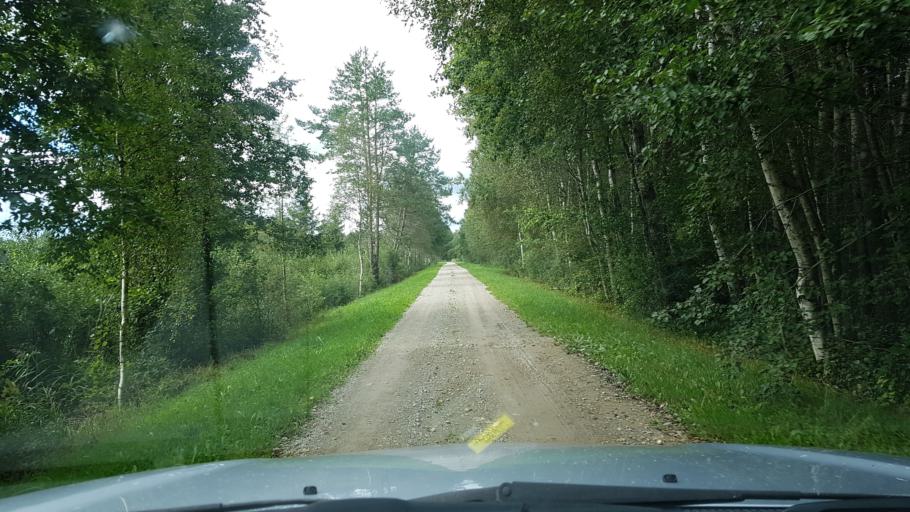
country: EE
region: Harju
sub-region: Raasiku vald
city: Arukula
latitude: 59.2922
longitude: 25.0587
